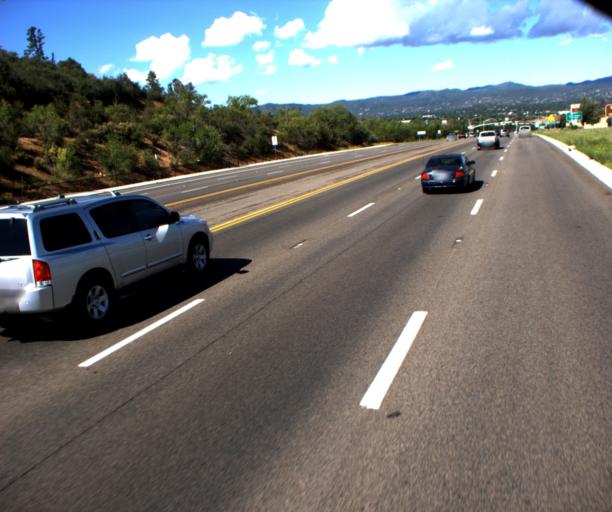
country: US
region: Arizona
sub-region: Yavapai County
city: Prescott
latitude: 34.5493
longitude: -112.4404
